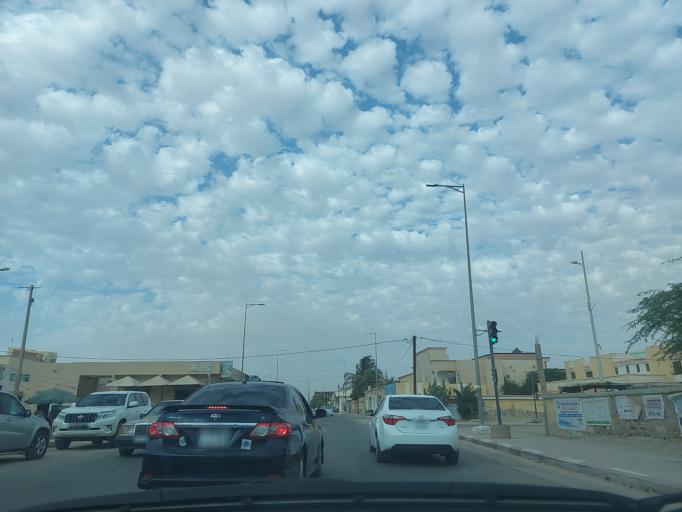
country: MR
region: Nouakchott
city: Nouakchott
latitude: 18.1096
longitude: -15.9942
